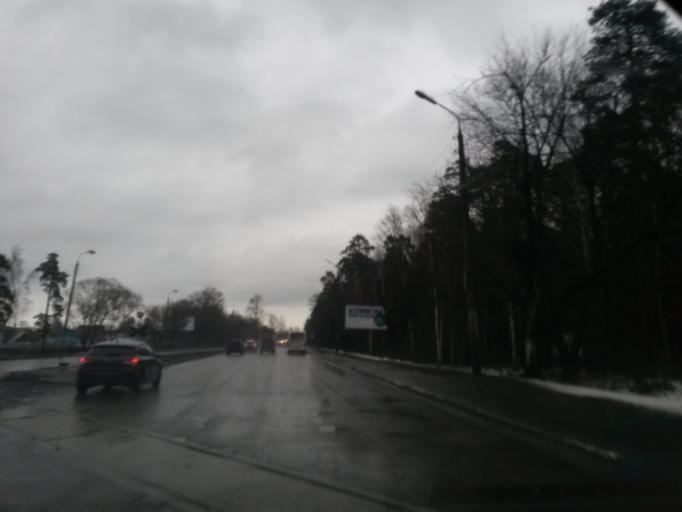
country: RU
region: Jaroslavl
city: Yaroslavl
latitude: 57.6468
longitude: 39.9232
